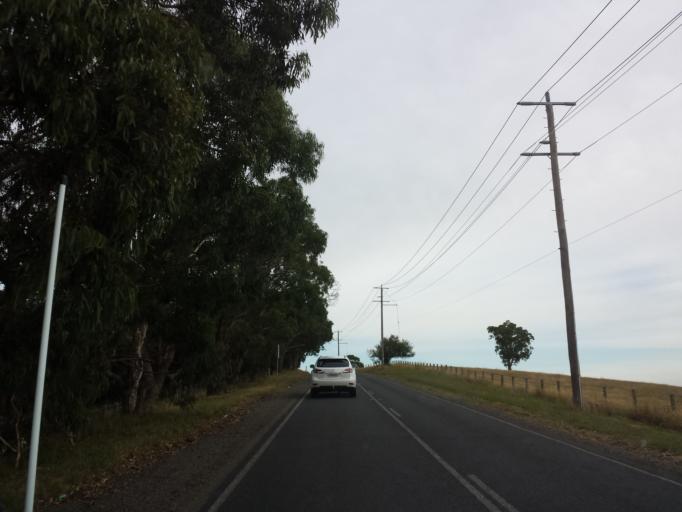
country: AU
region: Victoria
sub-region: Knox
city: Ferntree Gully
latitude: -37.9067
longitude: 145.3060
